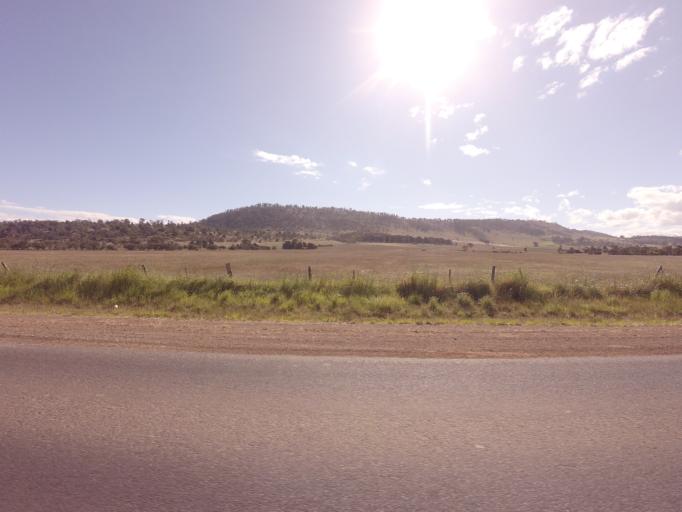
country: AU
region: Tasmania
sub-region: Clarence
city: Cambridge
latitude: -42.7104
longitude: 147.4300
